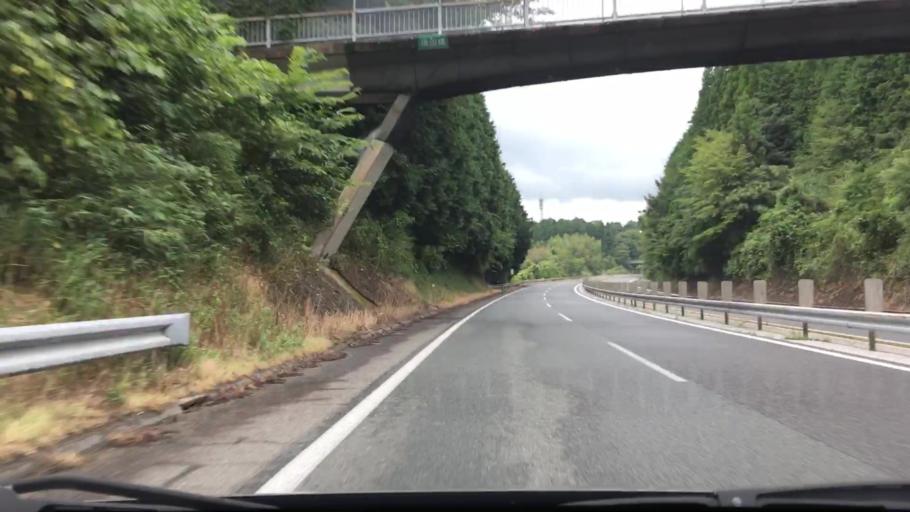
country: JP
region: Okayama
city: Niimi
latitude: 34.9301
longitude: 133.3271
